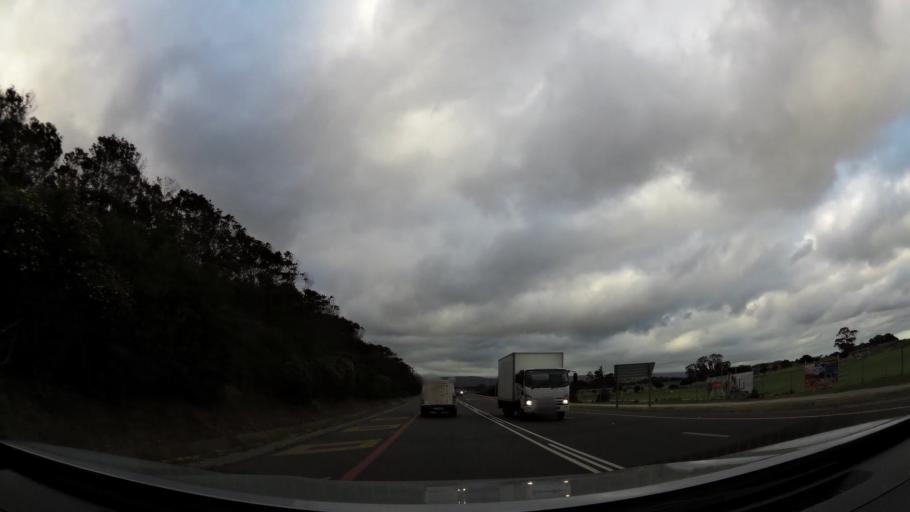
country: ZA
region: Western Cape
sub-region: Eden District Municipality
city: Plettenberg Bay
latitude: -34.0388
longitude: 23.3706
